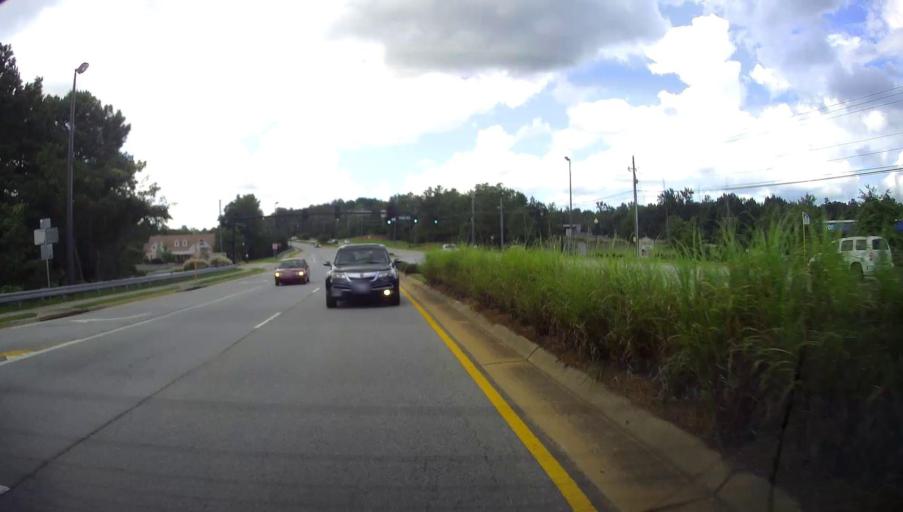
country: US
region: Alabama
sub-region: Russell County
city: Phenix City
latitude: 32.5555
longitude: -84.9271
